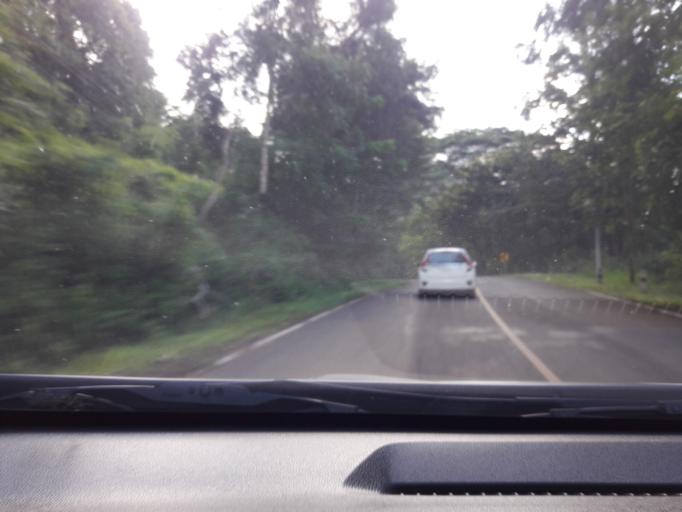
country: TH
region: Mae Hong Son
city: Sop Pong
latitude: 19.5604
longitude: 98.1929
